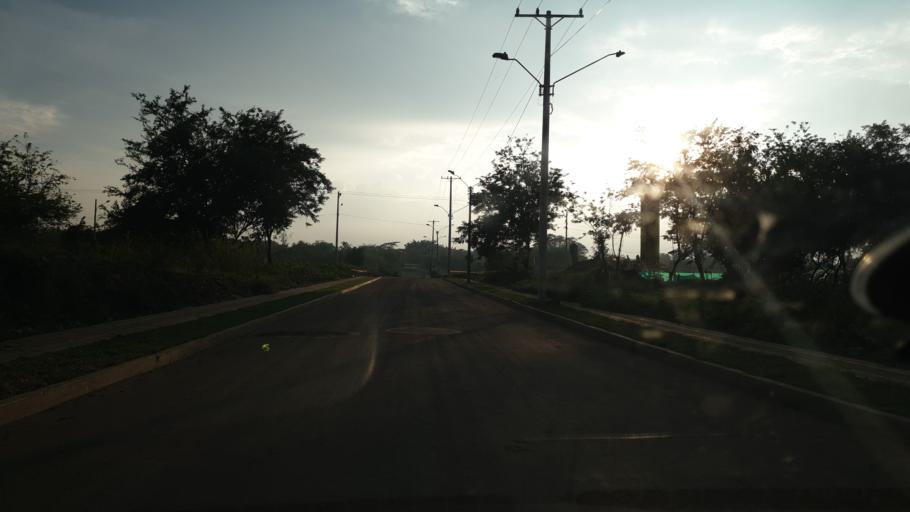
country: CO
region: Valle del Cauca
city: Jamundi
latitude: 3.3447
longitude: -76.5200
